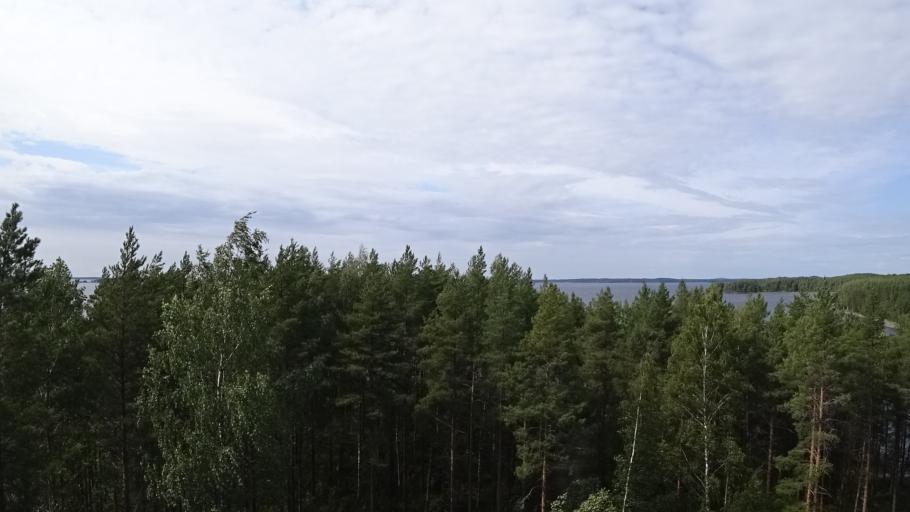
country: FI
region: North Karelia
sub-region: Keski-Karjala
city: Raeaekkylae
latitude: 62.3954
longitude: 29.7626
